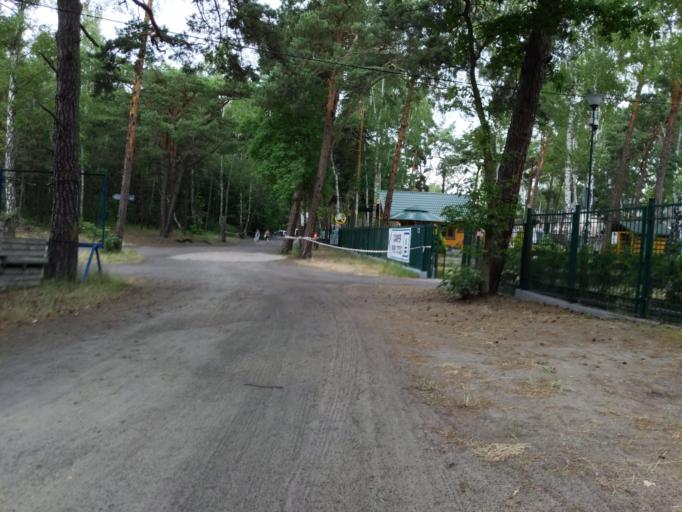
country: PL
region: Pomeranian Voivodeship
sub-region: Gdansk
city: Gdansk
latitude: 54.3701
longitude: 18.7301
